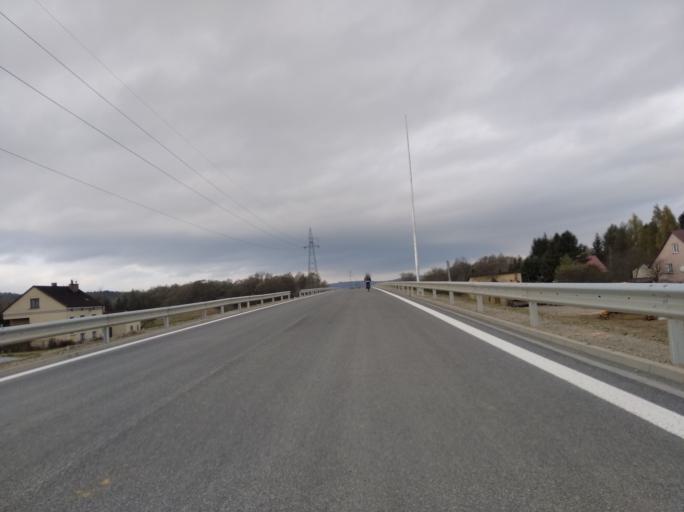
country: PL
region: Subcarpathian Voivodeship
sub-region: Powiat strzyzowski
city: Strzyzow
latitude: 49.8629
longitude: 21.7826
